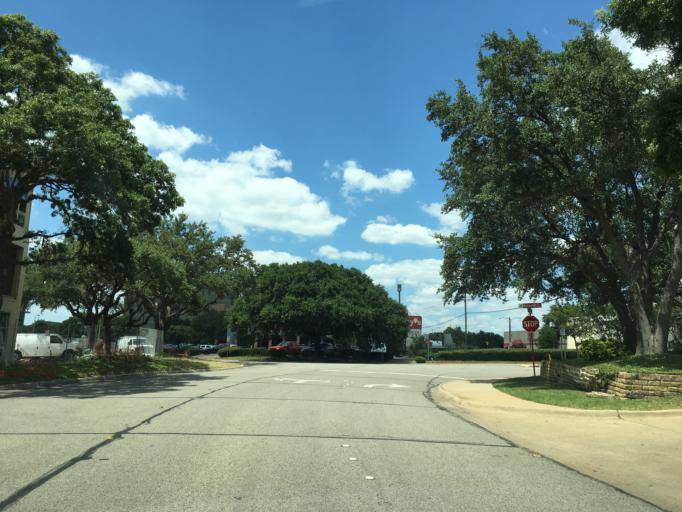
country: US
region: Texas
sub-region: Dallas County
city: Addison
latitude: 32.9285
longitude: -96.8396
